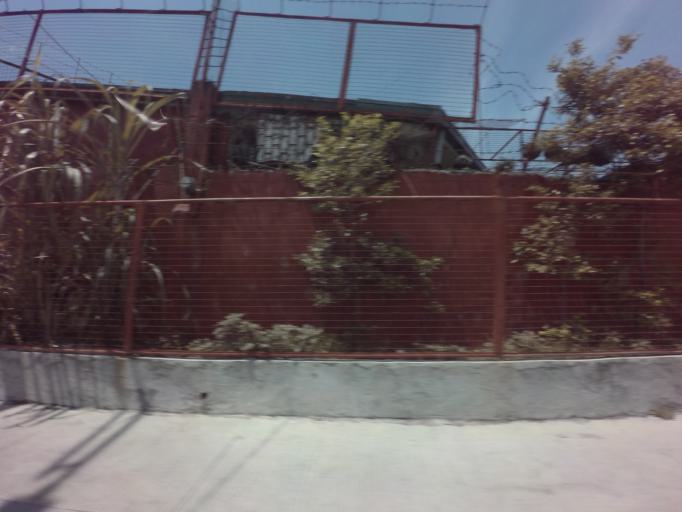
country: PH
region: Calabarzon
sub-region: Province of Rizal
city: Las Pinas
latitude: 14.4227
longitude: 120.9901
